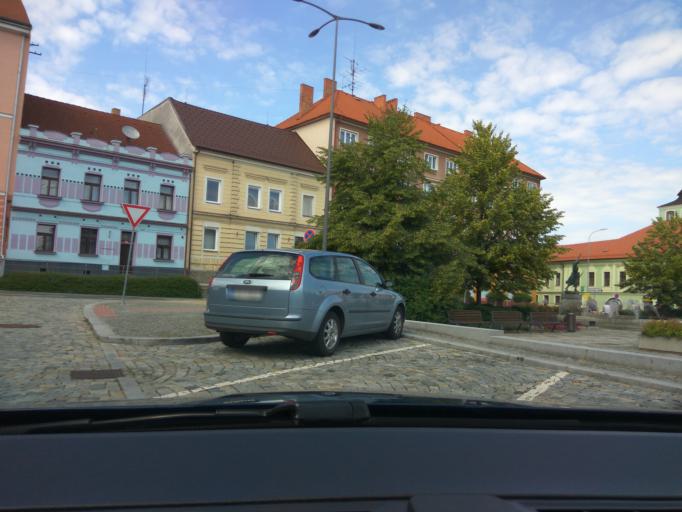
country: CZ
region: Jihocesky
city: Milevsko
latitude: 49.4506
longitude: 14.3592
